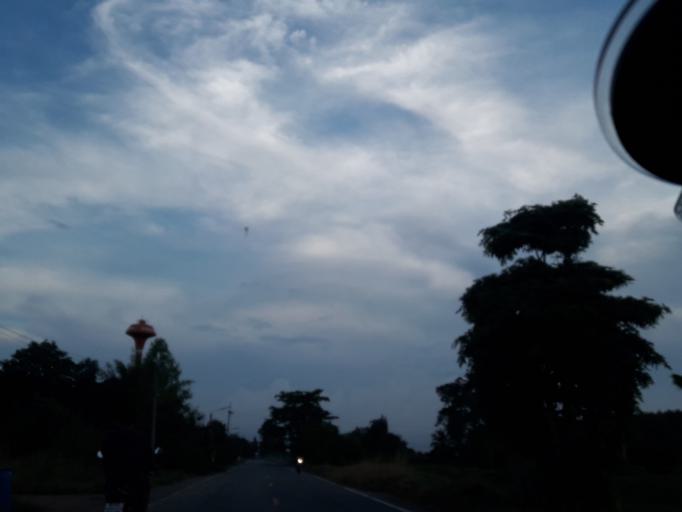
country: TH
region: Pathum Thani
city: Nong Suea
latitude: 14.1792
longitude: 100.8689
